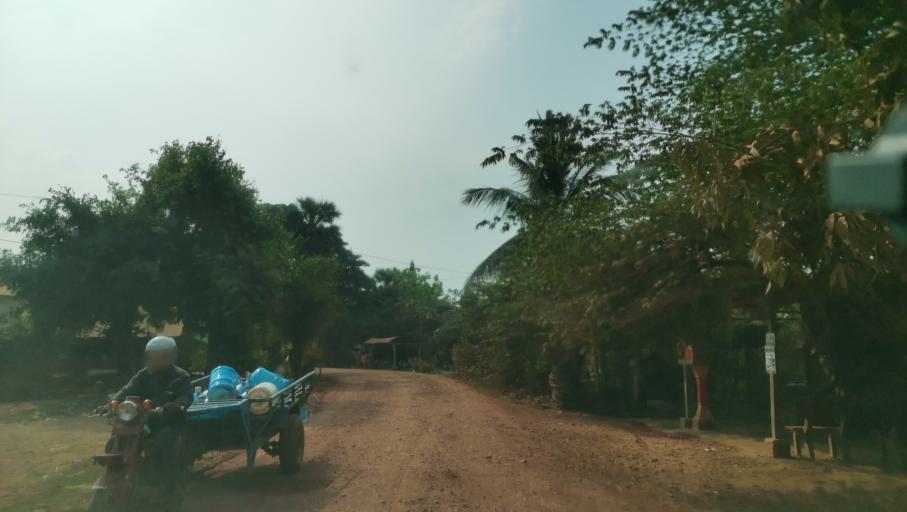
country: KH
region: Battambang
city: Battambang
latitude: 13.0553
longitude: 103.1698
